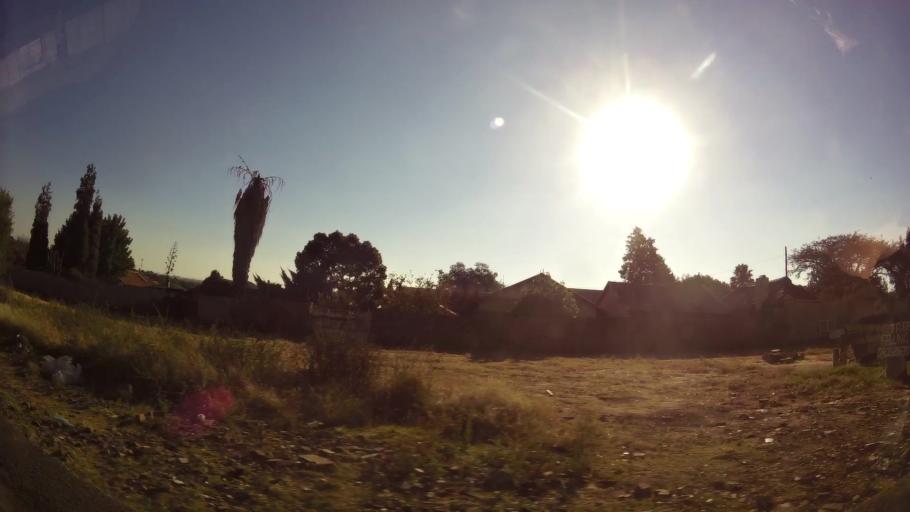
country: ZA
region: Gauteng
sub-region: City of Tshwane Metropolitan Municipality
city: Centurion
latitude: -25.8930
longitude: 28.1424
